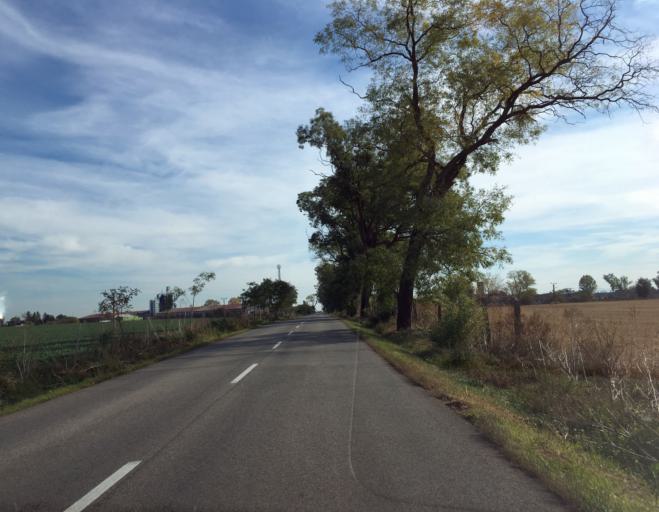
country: SK
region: Nitriansky
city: Zeliezovce
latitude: 48.0978
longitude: 18.5543
